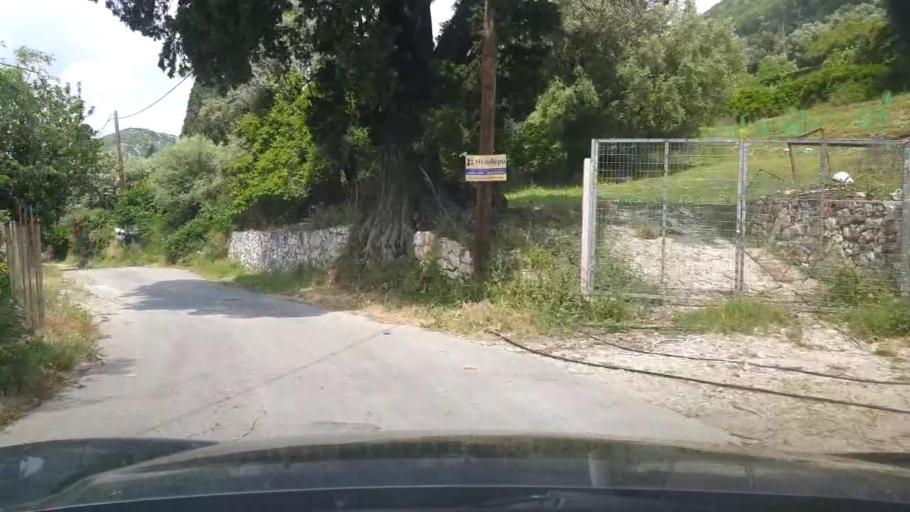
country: GR
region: Ionian Islands
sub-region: Lefkada
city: Nidri
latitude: 38.6430
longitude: 20.7060
